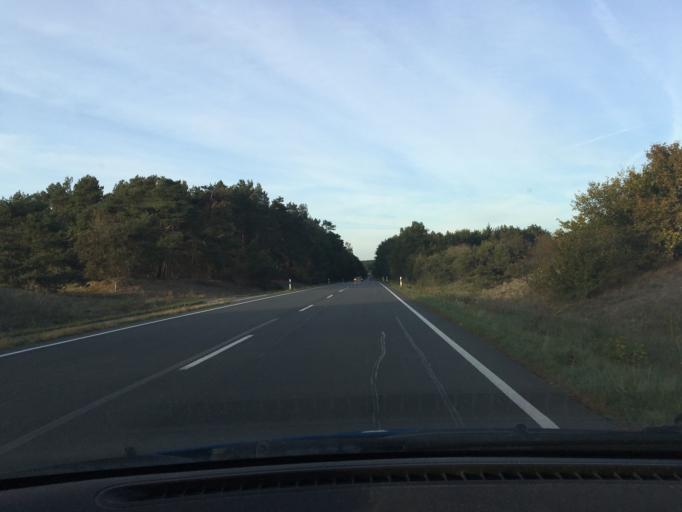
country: DE
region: Lower Saxony
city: Betzendorf
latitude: 53.1550
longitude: 10.2986
